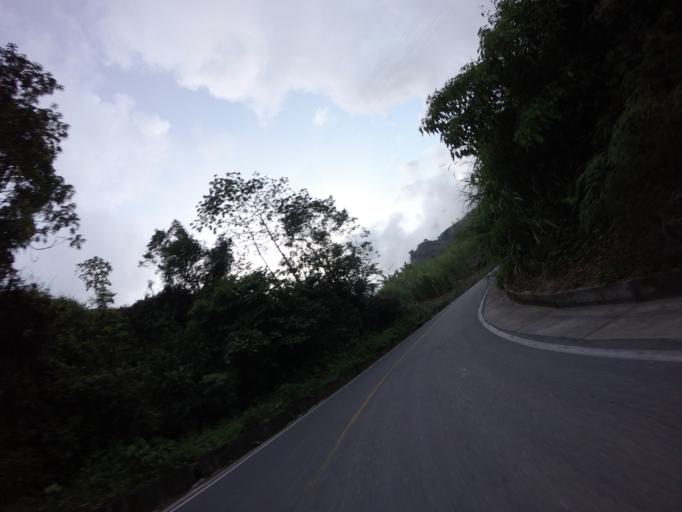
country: CO
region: Caldas
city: Manzanares
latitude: 5.3225
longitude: -75.1281
